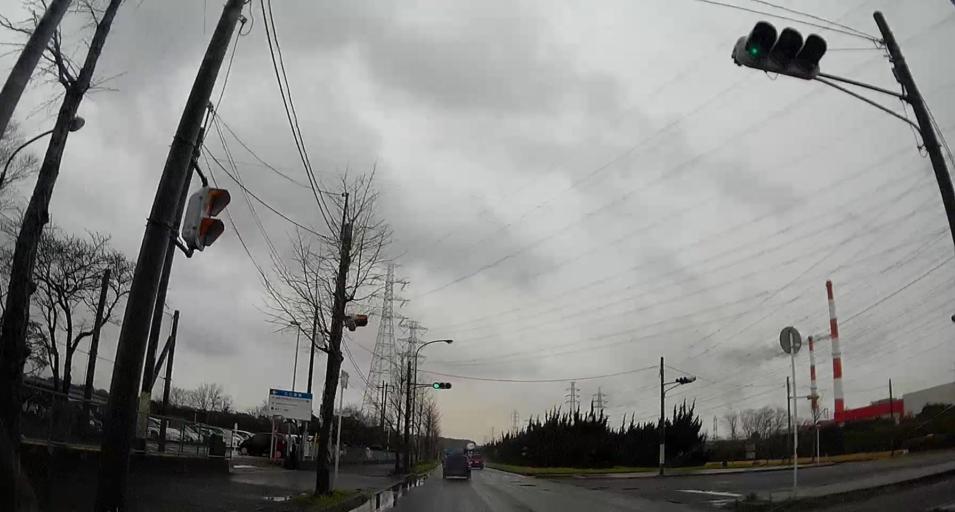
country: JP
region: Chiba
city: Ichihara
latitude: 35.4744
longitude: 140.0304
